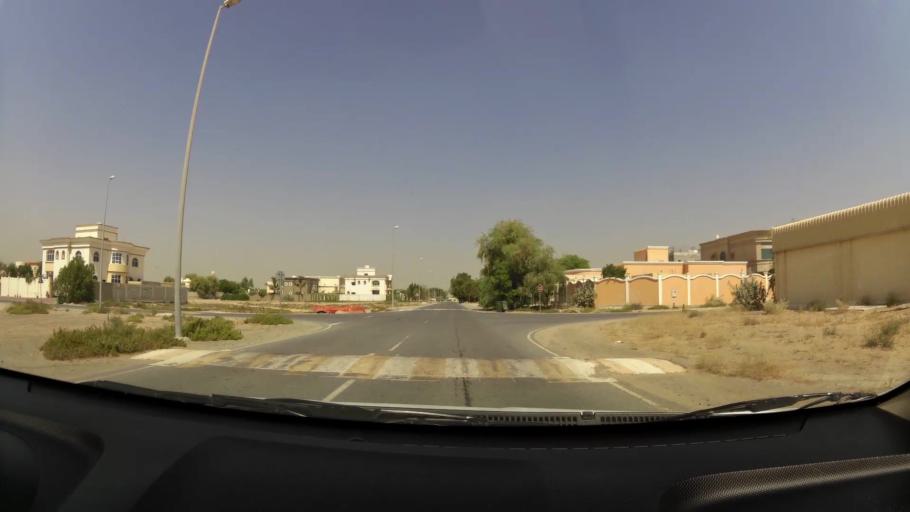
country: AE
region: Ajman
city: Ajman
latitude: 25.3954
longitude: 55.5405
